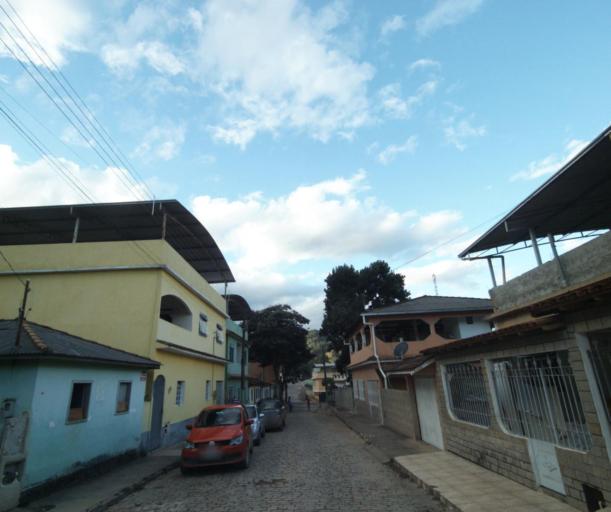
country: BR
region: Espirito Santo
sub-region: Guacui
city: Guacui
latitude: -20.6215
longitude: -41.6862
